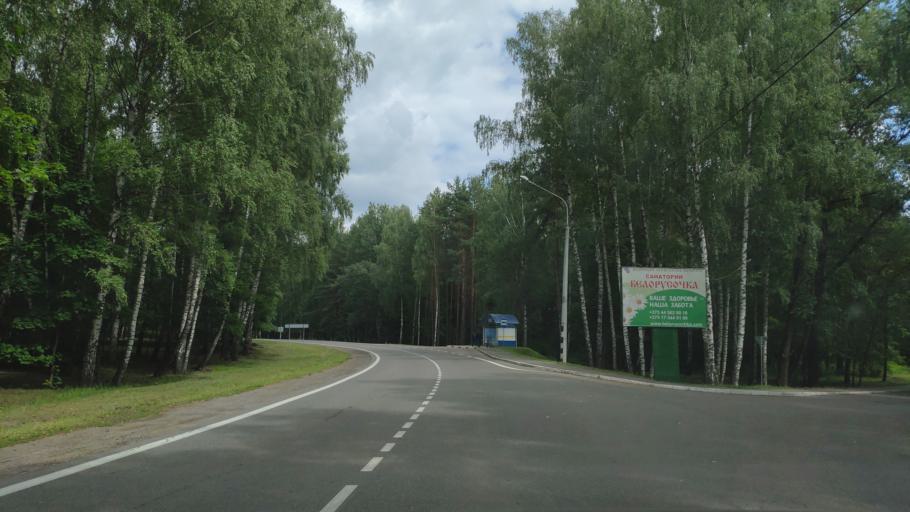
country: BY
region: Minsk
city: Zhdanovichy
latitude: 53.9685
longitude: 27.4291
